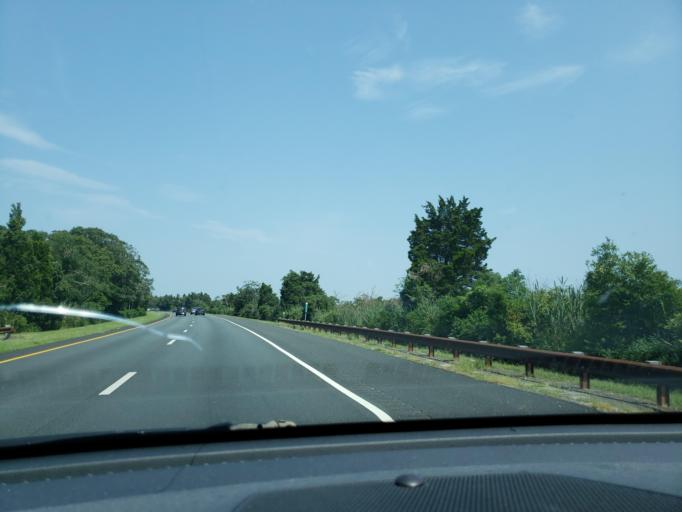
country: US
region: New Jersey
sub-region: Cape May County
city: Ocean City
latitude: 39.2725
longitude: -74.6318
